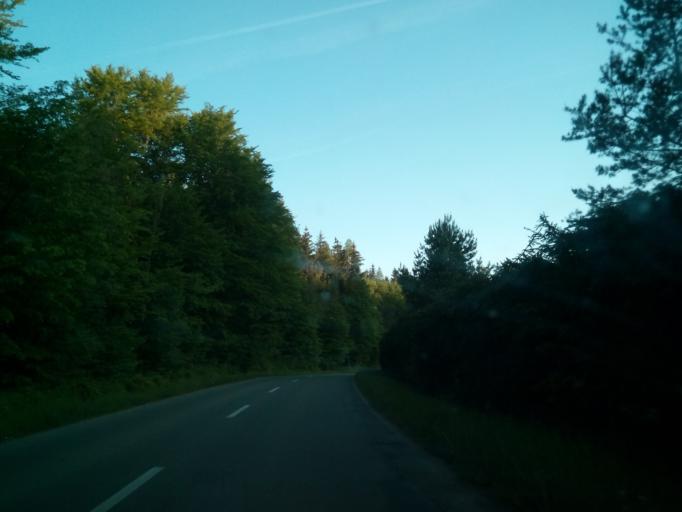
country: CZ
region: South Moravian
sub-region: Okres Blansko
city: Jedovnice
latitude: 49.3080
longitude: 16.7465
